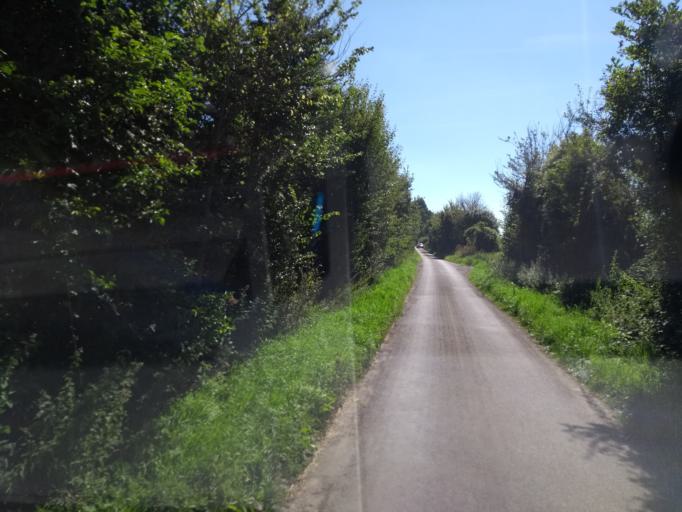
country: GB
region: England
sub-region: Somerset
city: Ilchester
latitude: 51.0549
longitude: -2.6869
